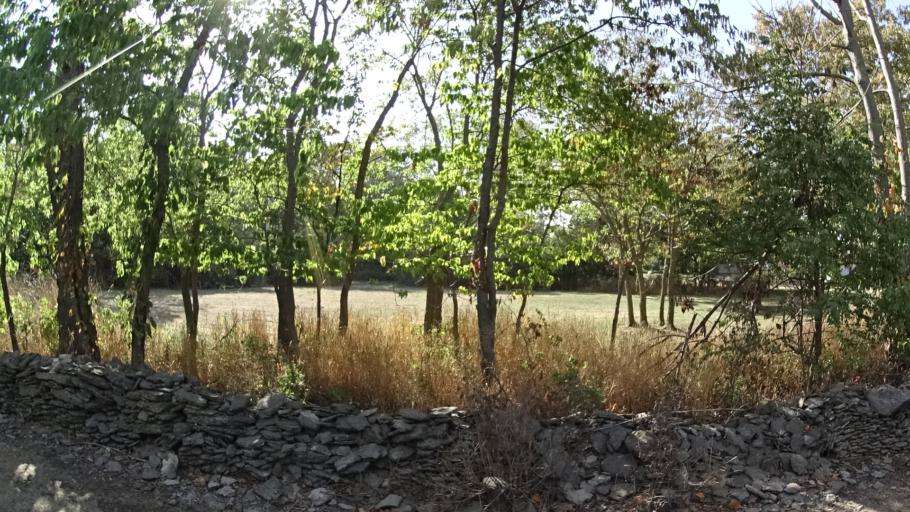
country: US
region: Ohio
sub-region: Erie County
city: Sandusky
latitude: 41.6158
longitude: -82.6846
